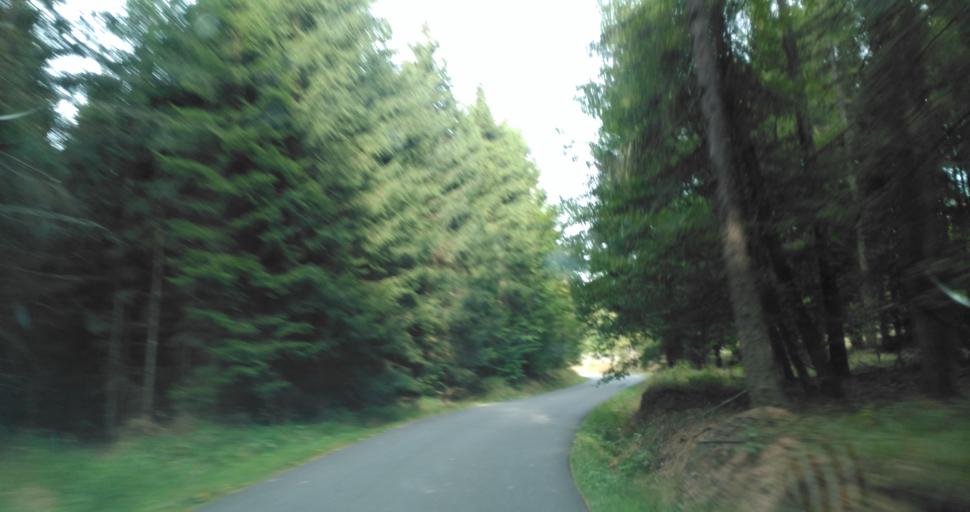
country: CZ
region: Plzensky
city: Zbiroh
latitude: 49.9258
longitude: 13.7993
